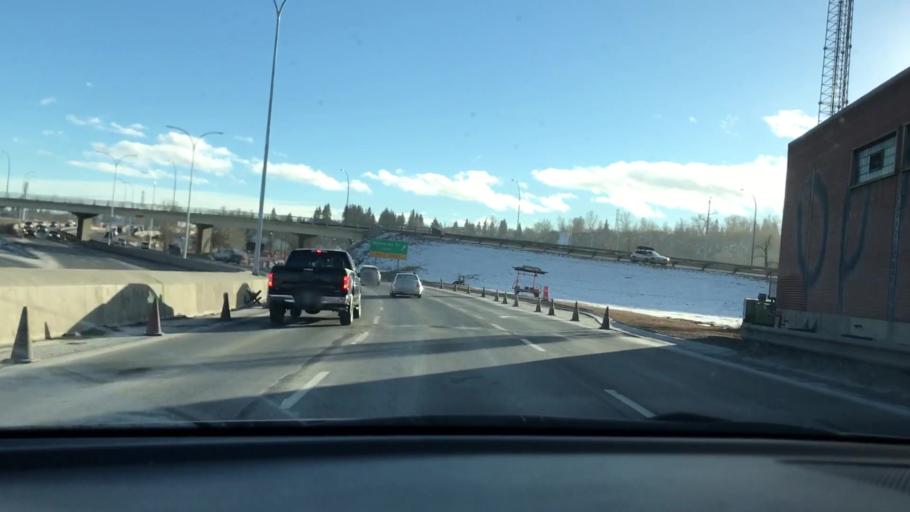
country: CA
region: Alberta
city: Calgary
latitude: 51.0510
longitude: -114.1180
